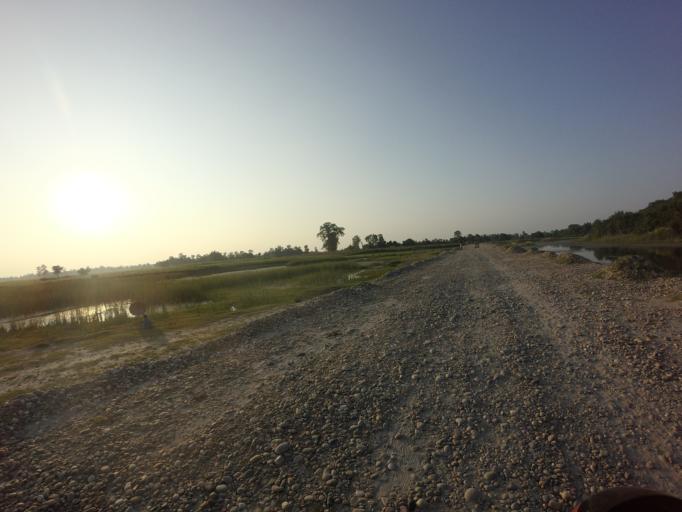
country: NP
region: Far Western
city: Tikapur
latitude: 28.4482
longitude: 81.0743
